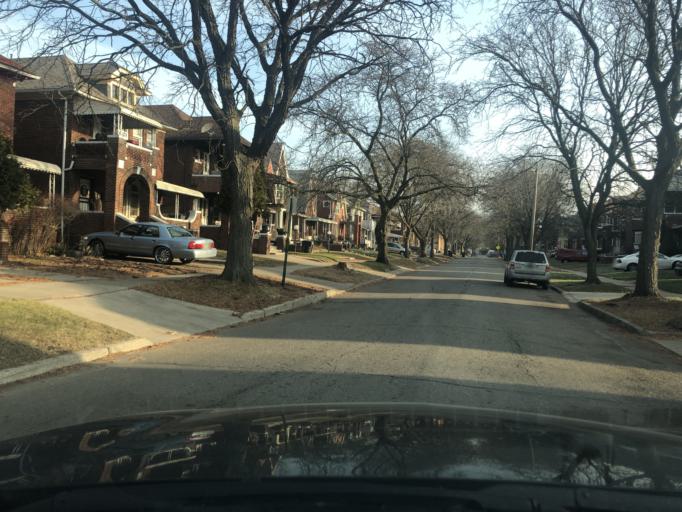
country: US
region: Michigan
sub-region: Wayne County
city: Highland Park
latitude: 42.3866
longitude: -83.1243
